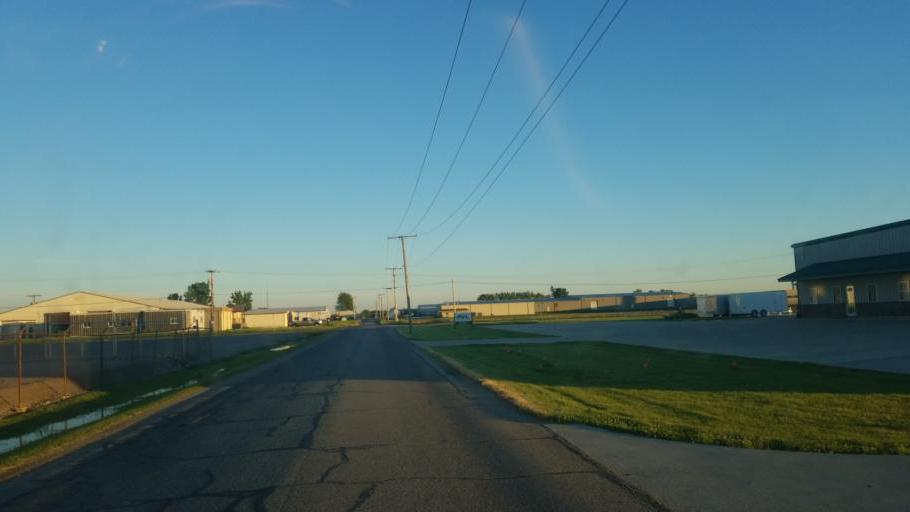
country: US
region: Indiana
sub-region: Elkhart County
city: Nappanee
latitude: 41.4490
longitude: -86.0304
